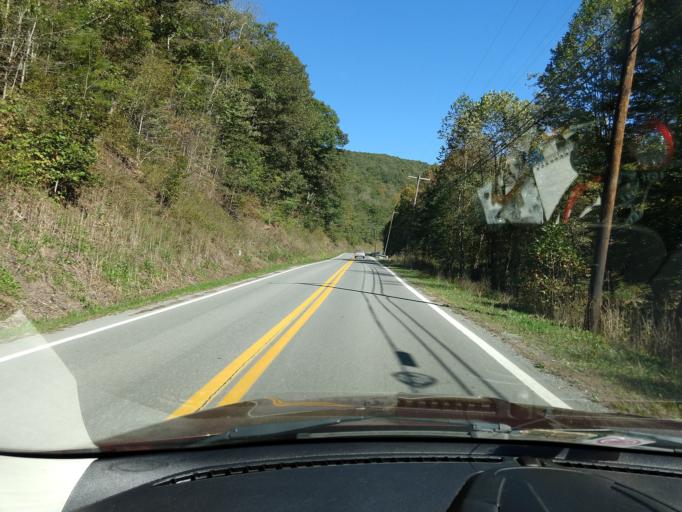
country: US
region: West Virginia
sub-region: Pocahontas County
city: Marlinton
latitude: 38.2130
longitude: -80.0689
